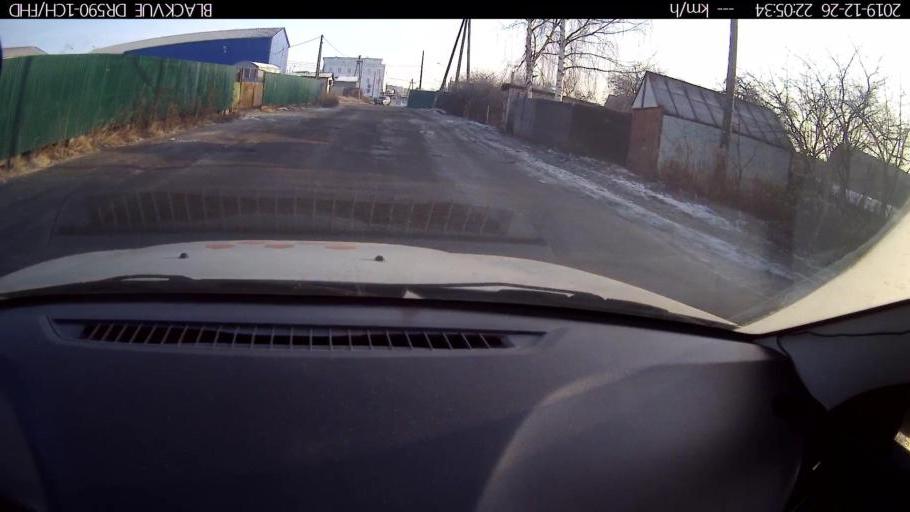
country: RU
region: Nizjnij Novgorod
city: Afonino
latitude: 56.1963
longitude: 44.0916
